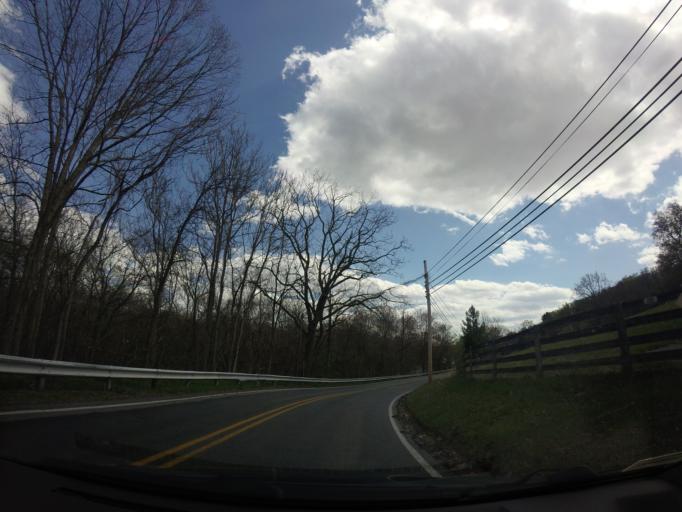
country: US
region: Maryland
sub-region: Washington County
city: Keedysville
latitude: 39.4390
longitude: -77.6807
